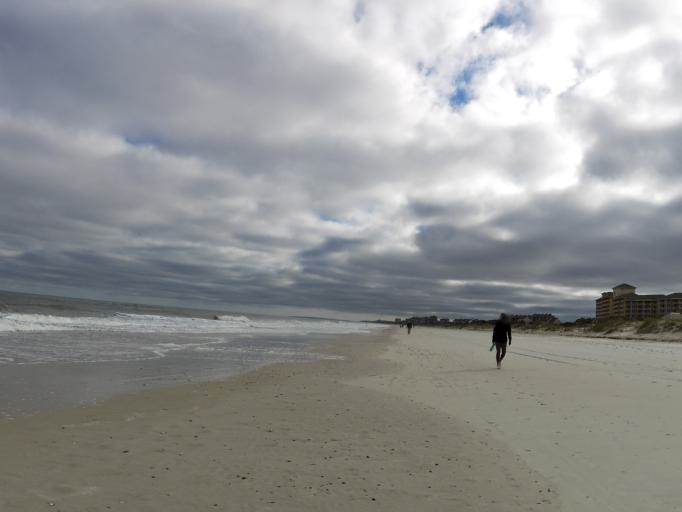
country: US
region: Florida
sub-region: Nassau County
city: Fernandina Beach
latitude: 30.5576
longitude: -81.4421
